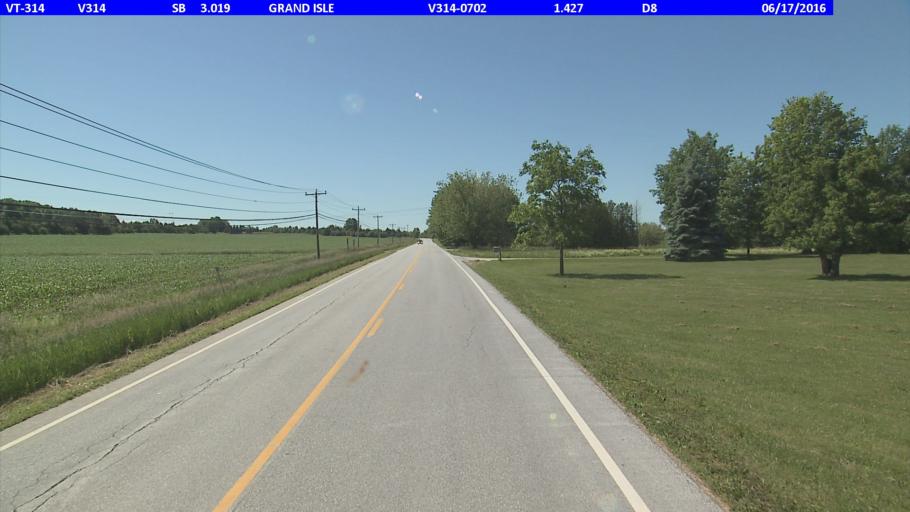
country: US
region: New York
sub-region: Clinton County
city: Cumberland Head
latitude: 44.6980
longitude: -73.3483
